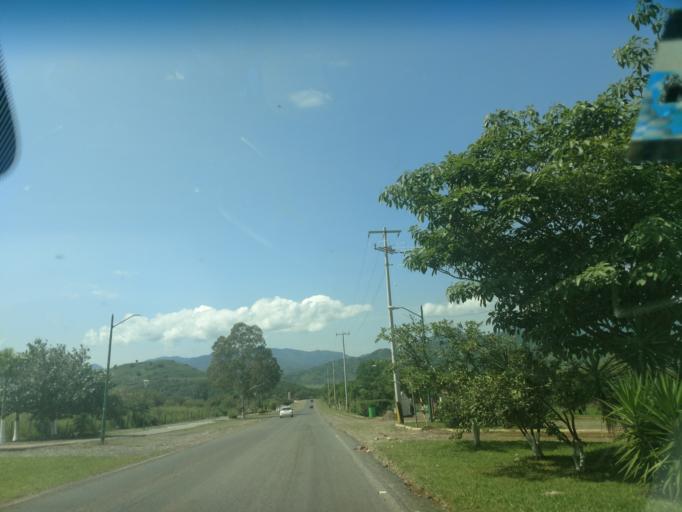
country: MX
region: Jalisco
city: Talpa de Allende
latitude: 20.3996
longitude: -104.8152
